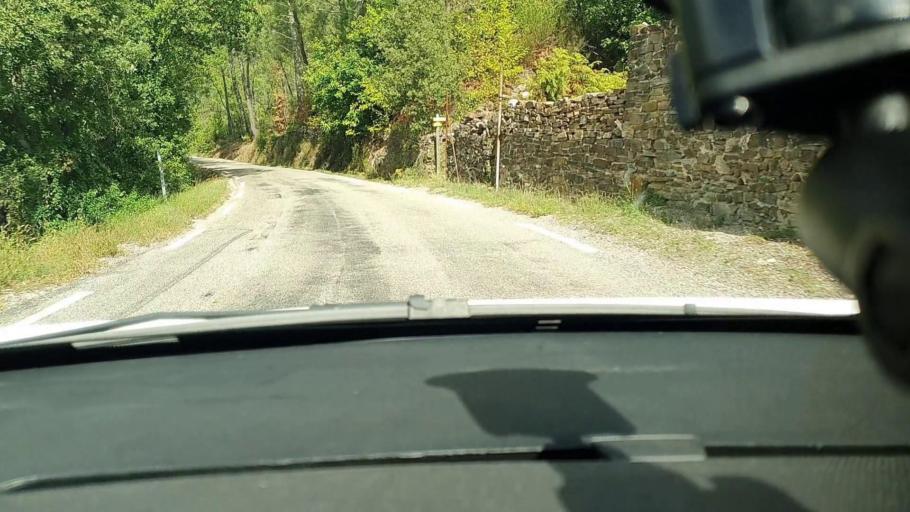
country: FR
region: Languedoc-Roussillon
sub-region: Departement du Gard
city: Besseges
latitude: 44.3080
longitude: 4.0582
